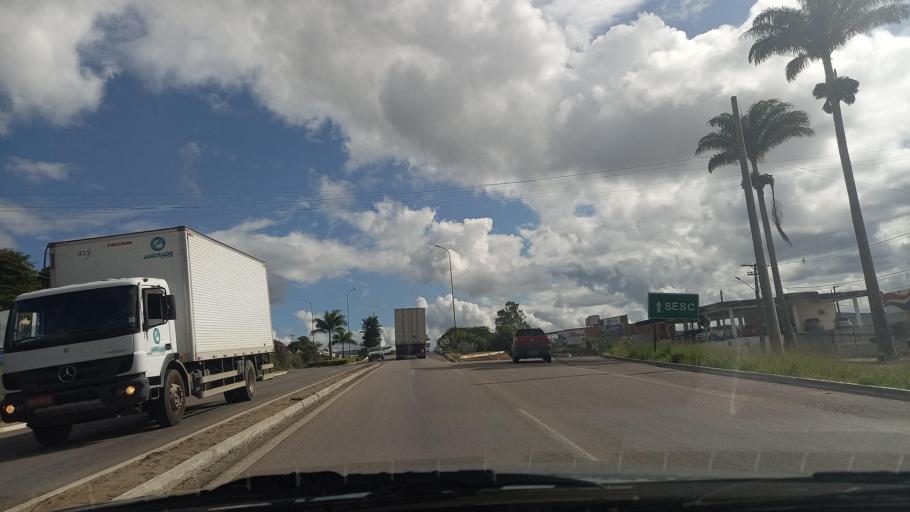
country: BR
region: Pernambuco
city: Garanhuns
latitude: -8.8756
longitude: -36.4720
